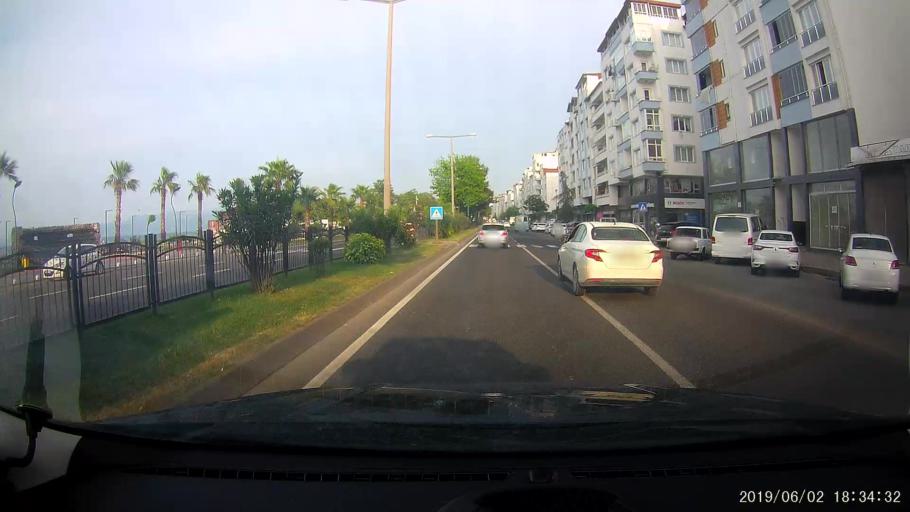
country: TR
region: Ordu
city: Fatsa
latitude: 41.0290
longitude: 37.5053
